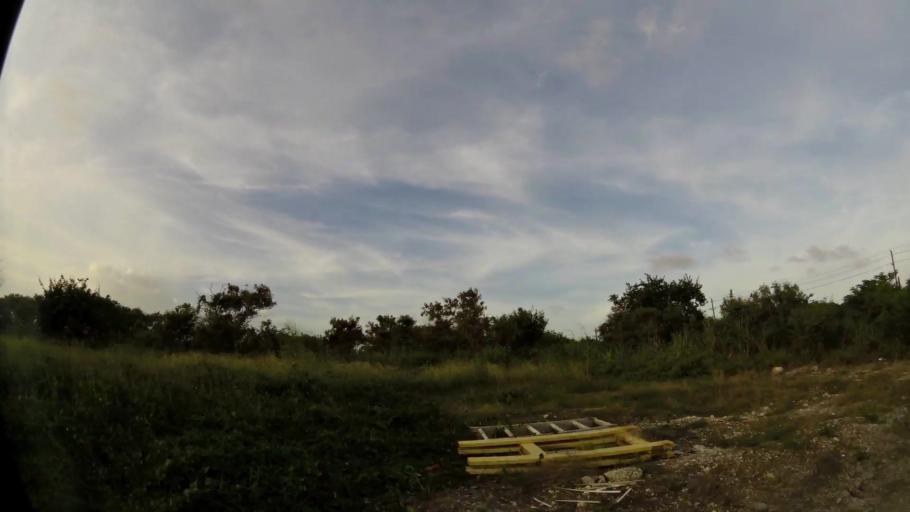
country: BB
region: Saint Philip
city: Crane
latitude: 13.0874
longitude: -59.4929
